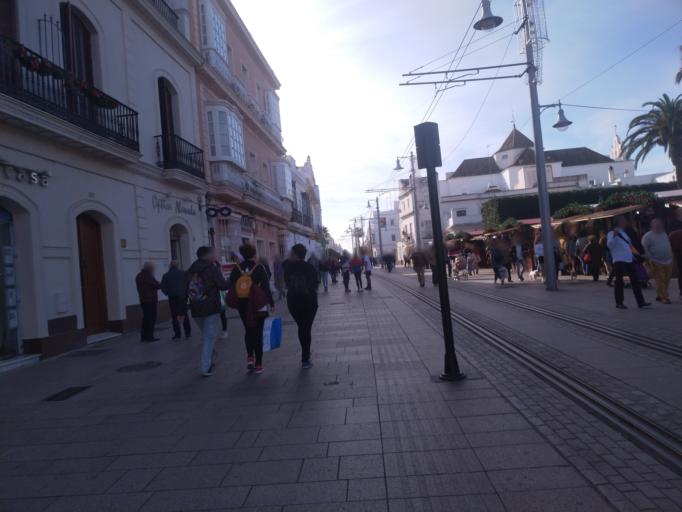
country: ES
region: Andalusia
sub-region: Provincia de Cadiz
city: San Fernando
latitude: 36.4632
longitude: -6.1997
